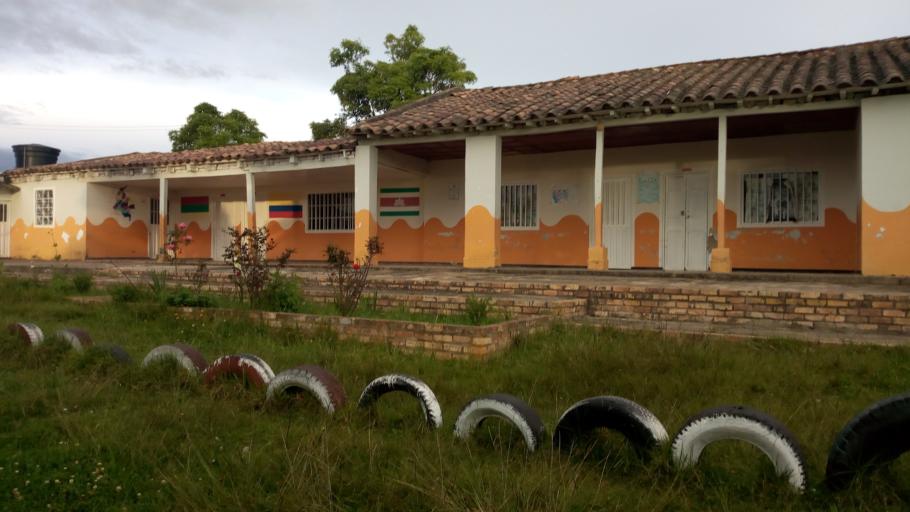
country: CO
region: Boyaca
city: Toca
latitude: 5.5852
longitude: -73.1710
